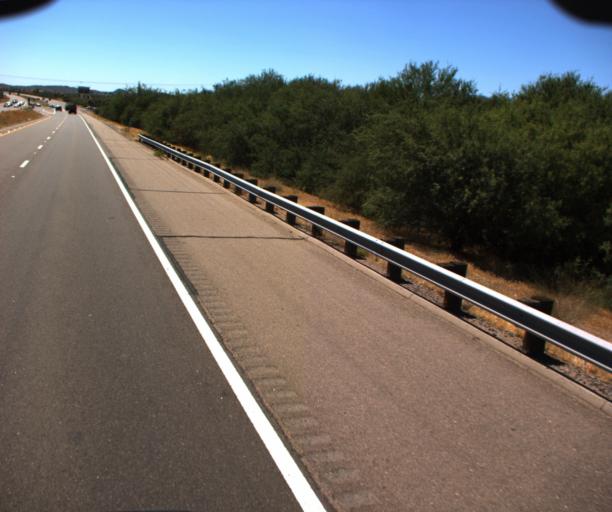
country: US
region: Arizona
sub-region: Maricopa County
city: Fountain Hills
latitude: 33.5806
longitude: -111.6746
